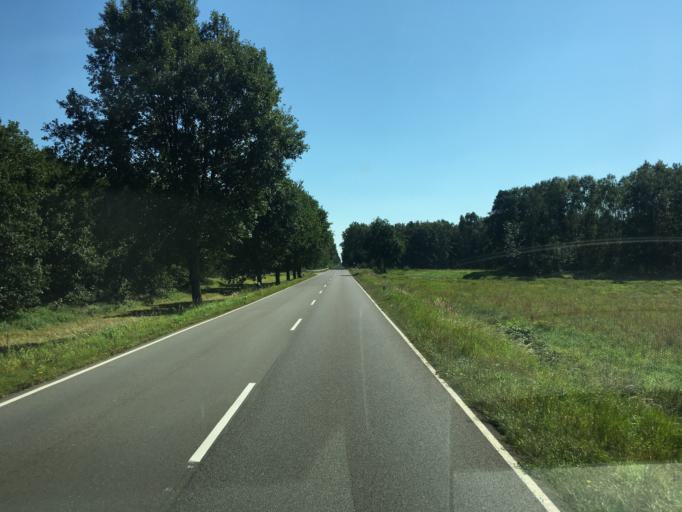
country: DE
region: Brandenburg
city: Welzow
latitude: 51.5416
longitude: 14.1801
